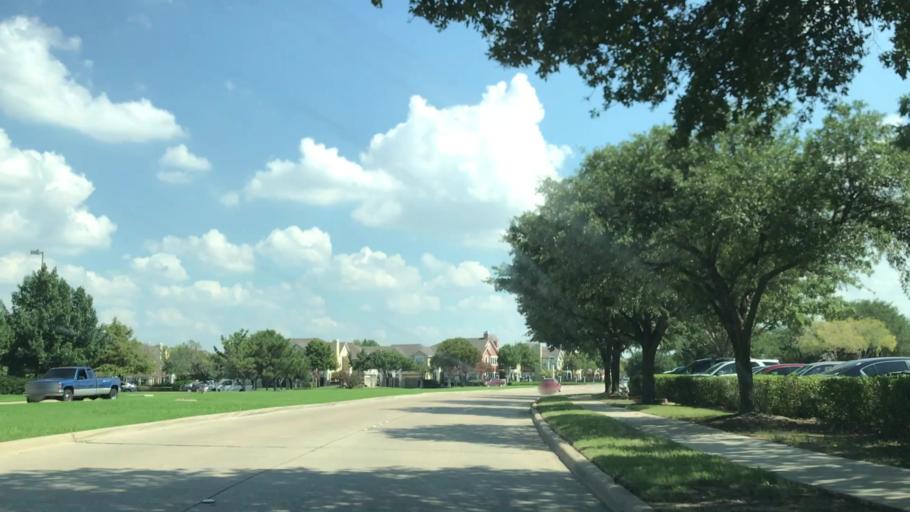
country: US
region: Texas
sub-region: Denton County
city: Lewisville
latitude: 33.0147
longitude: -96.9719
